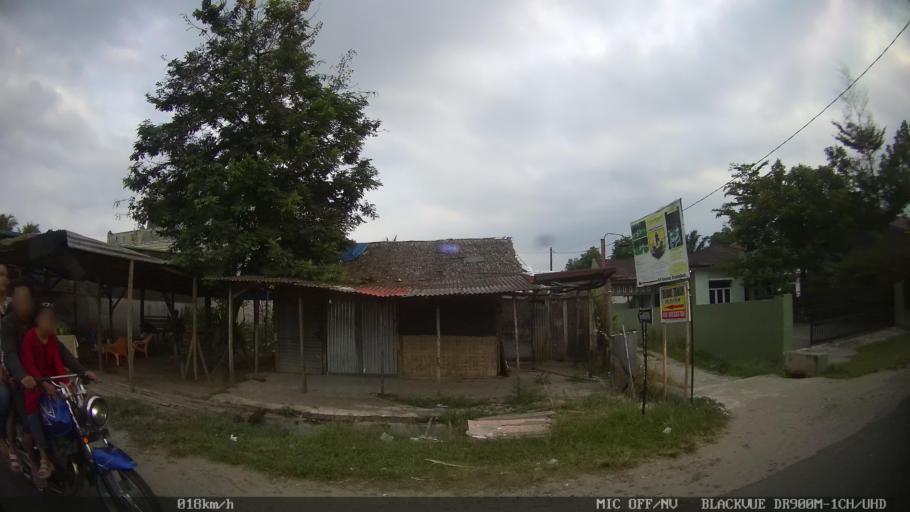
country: ID
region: North Sumatra
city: Sunggal
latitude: 3.5591
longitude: 98.5569
